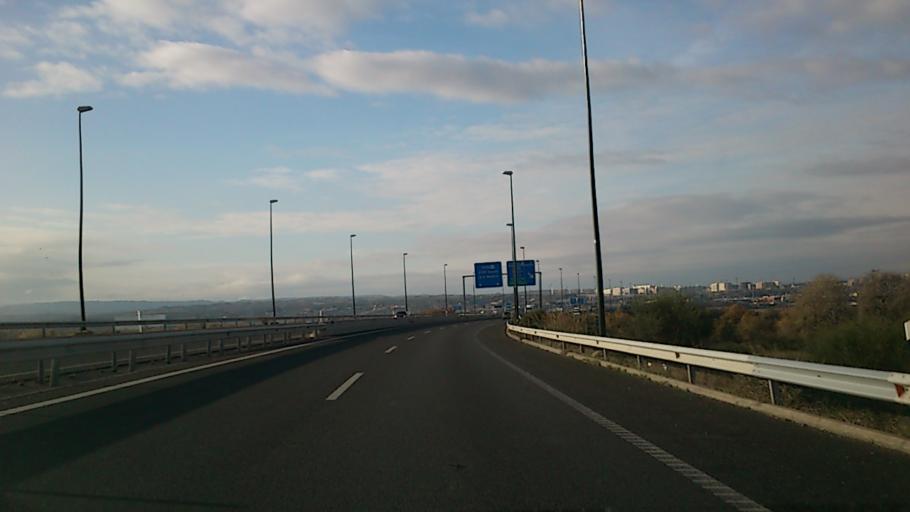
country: ES
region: Aragon
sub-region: Provincia de Zaragoza
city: Zaragoza
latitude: 41.6343
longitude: -0.8346
